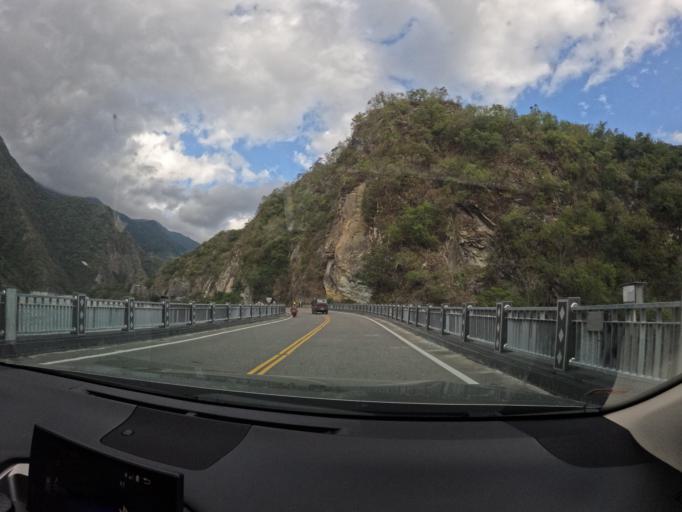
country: TW
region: Taiwan
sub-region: Taitung
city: Taitung
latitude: 23.1334
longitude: 121.1195
